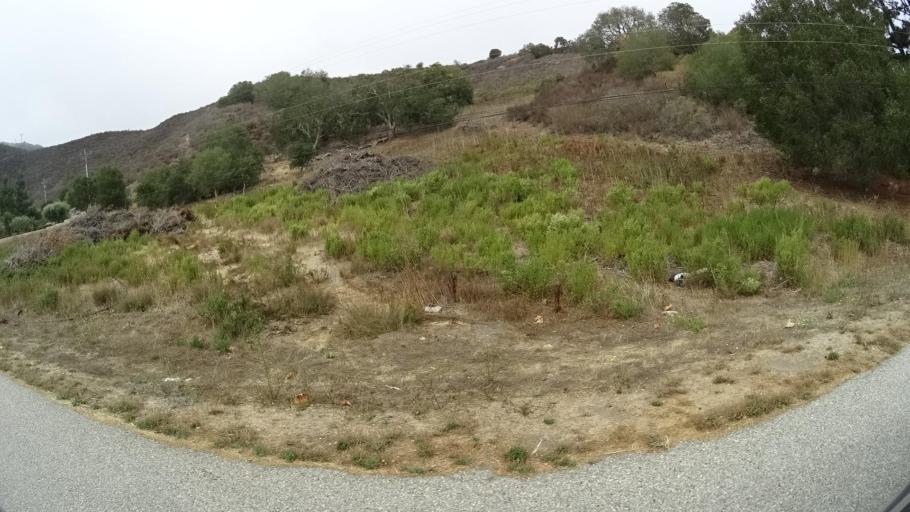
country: US
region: California
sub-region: Monterey County
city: Carmel Valley Village
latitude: 36.5604
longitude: -121.7551
